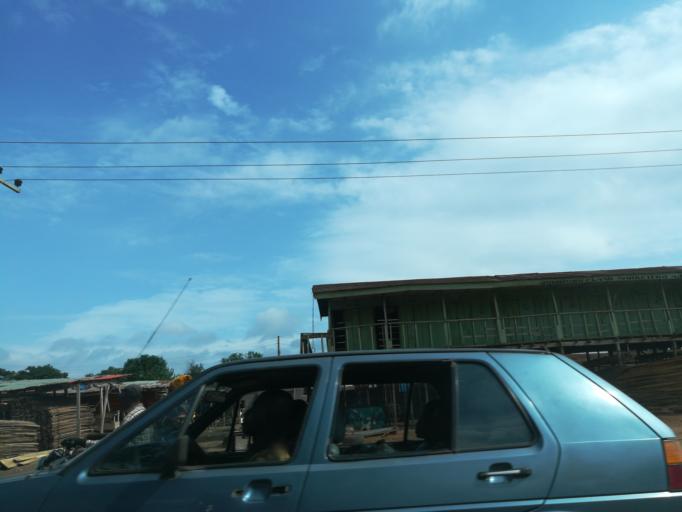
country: NG
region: Lagos
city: Ikorodu
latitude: 6.6315
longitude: 3.5298
